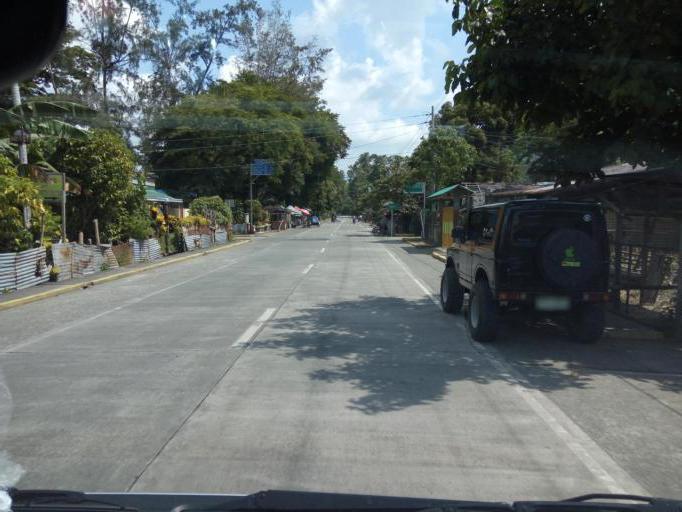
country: PH
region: Central Luzon
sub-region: Province of Aurora
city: Maria Aurora
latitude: 15.7984
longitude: 121.4753
